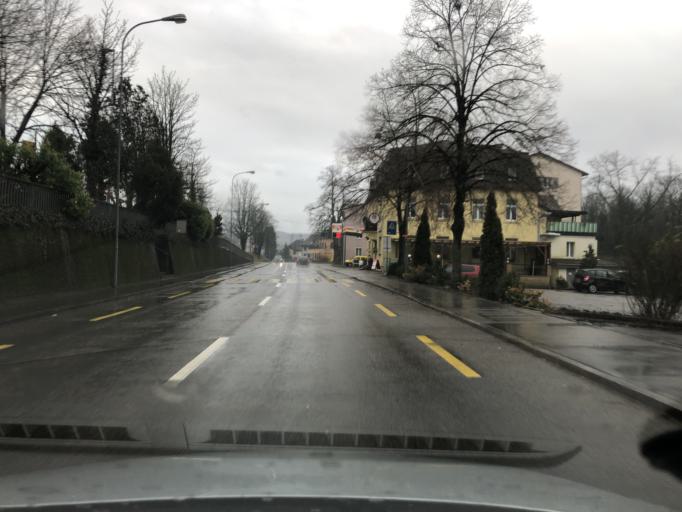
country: CH
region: Aargau
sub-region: Bezirk Zurzach
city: Koblenz
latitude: 47.6007
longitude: 8.2266
